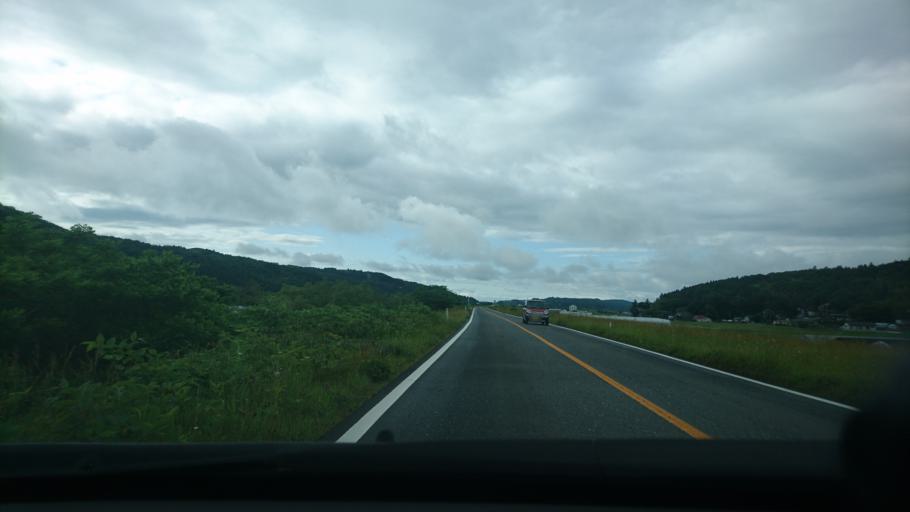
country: JP
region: Miyagi
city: Wakuya
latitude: 38.6296
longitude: 141.2921
